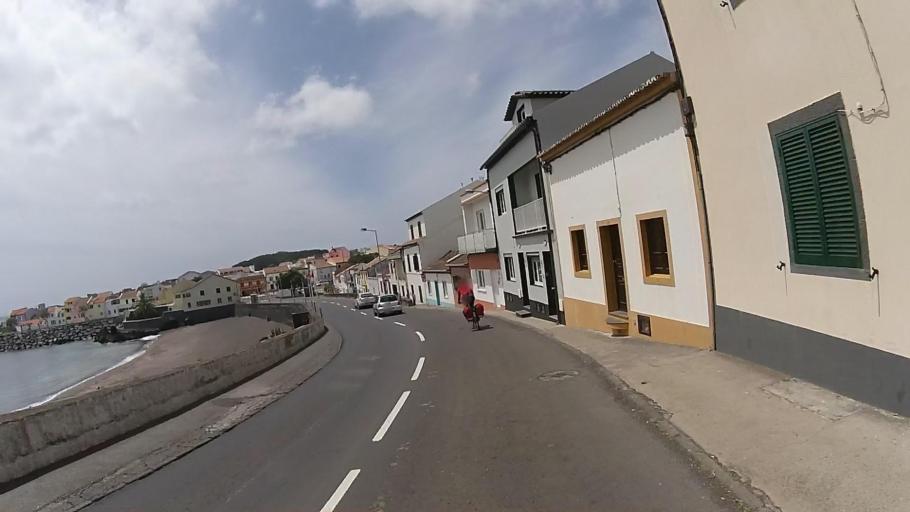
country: PT
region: Azores
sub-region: Ponta Delgada
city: Rosto de Cao
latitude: 37.7506
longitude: -25.6307
